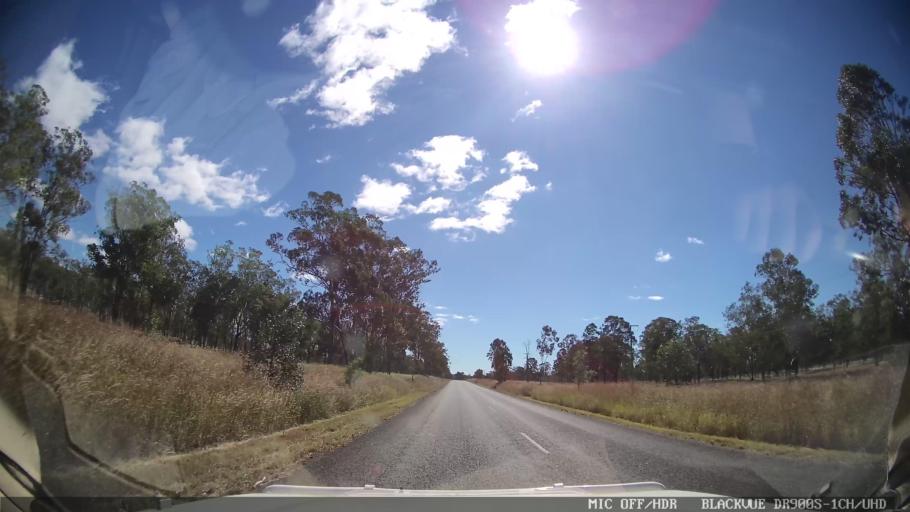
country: AU
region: Queensland
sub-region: Gladstone
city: Toolooa
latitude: -24.4427
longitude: 151.3413
